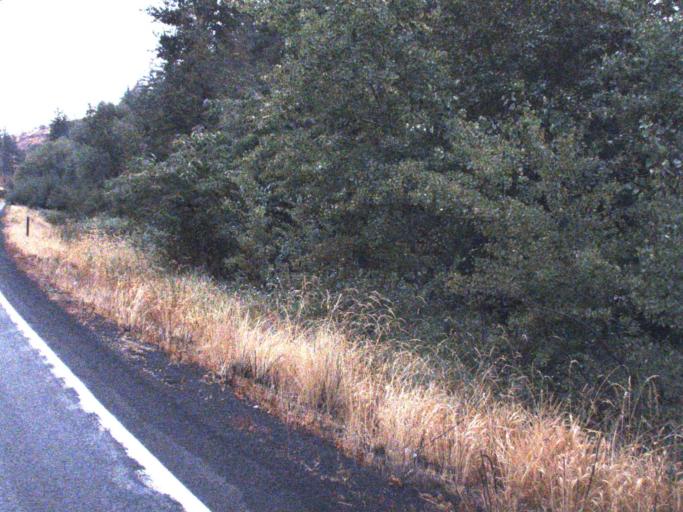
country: US
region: Washington
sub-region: Spokane County
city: Medical Lake
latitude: 47.7505
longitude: -117.8875
